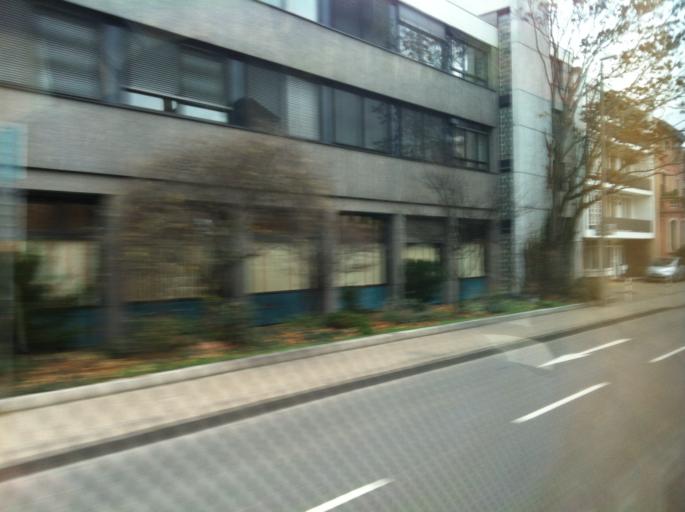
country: DE
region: Rheinland-Pfalz
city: Bad Kreuznach
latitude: 49.8353
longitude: 7.8536
